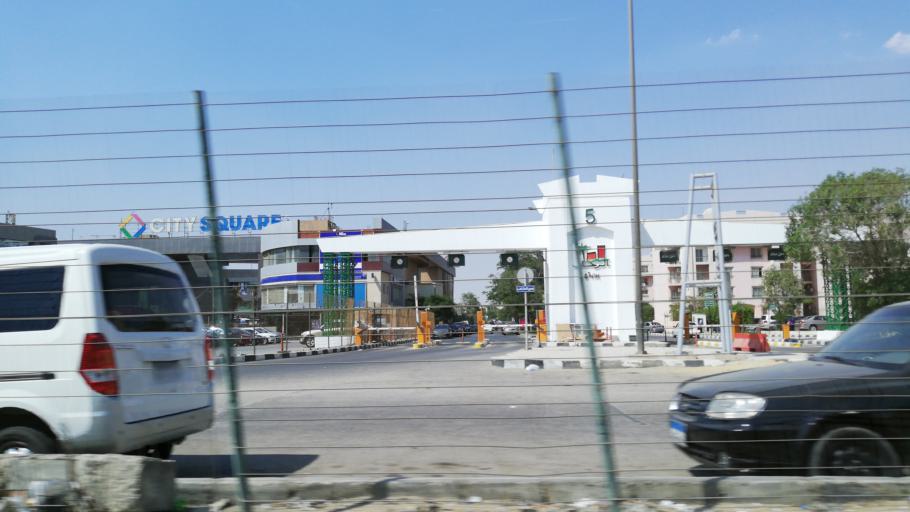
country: EG
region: Muhafazat al Qalyubiyah
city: Al Khankah
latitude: 30.0535
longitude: 31.4930
